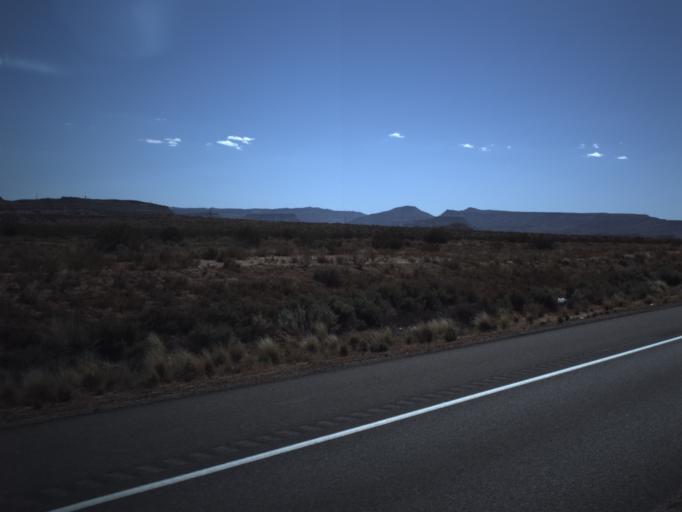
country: US
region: Utah
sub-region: Washington County
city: Washington
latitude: 37.0378
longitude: -113.4852
